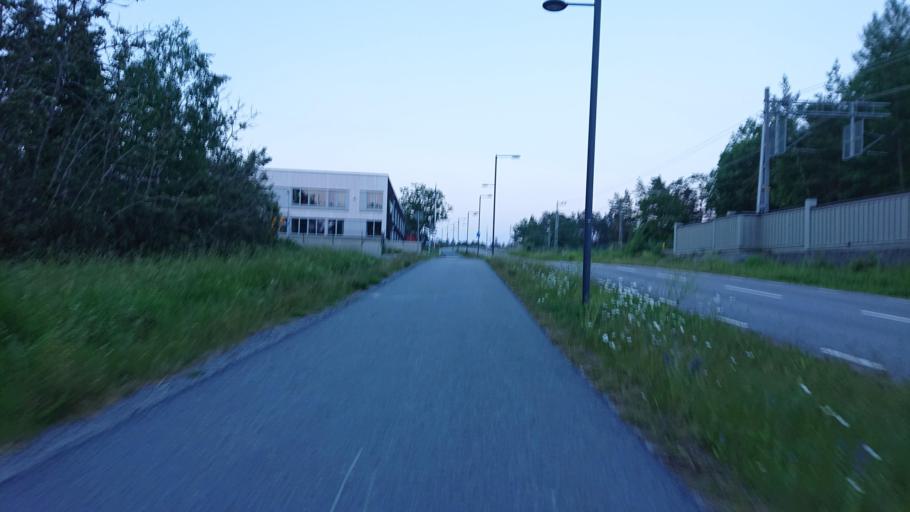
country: SE
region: Stockholm
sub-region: Osterakers Kommun
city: Akersberga
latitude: 59.4767
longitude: 18.2490
